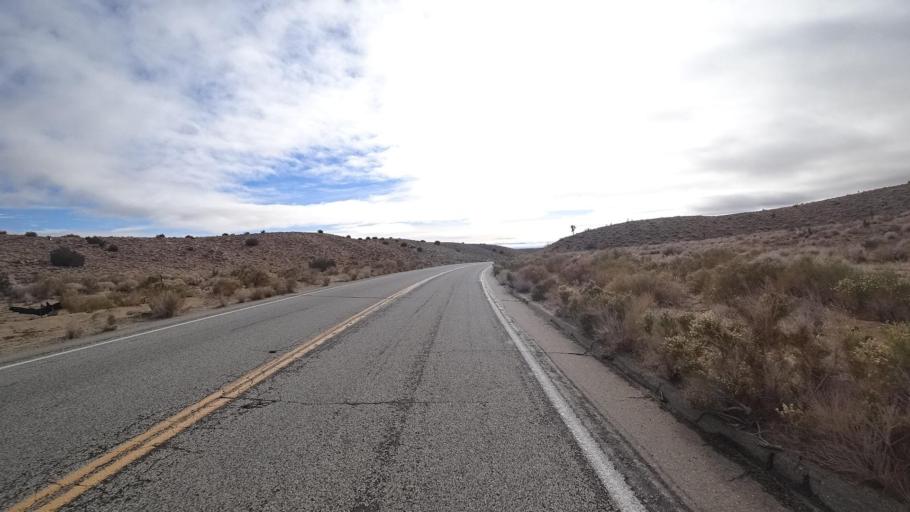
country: US
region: California
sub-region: Kern County
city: Tehachapi
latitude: 35.0106
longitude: -118.3419
